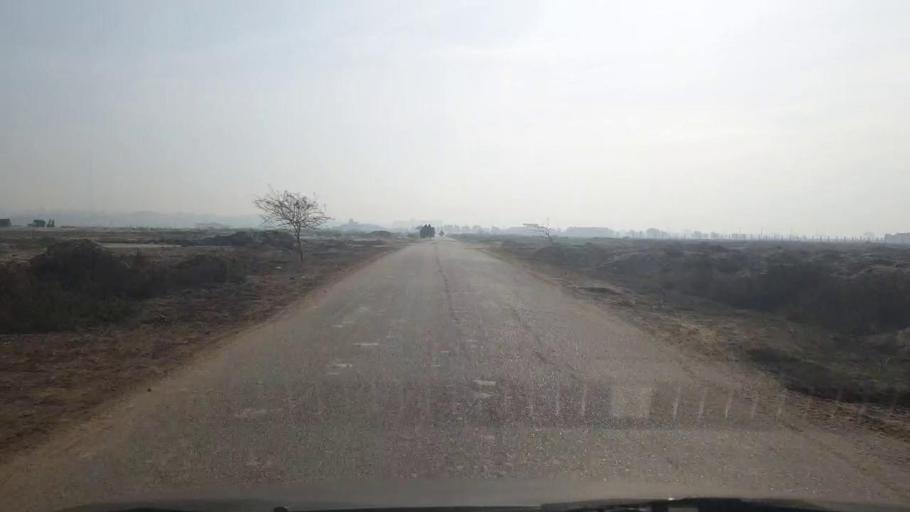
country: PK
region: Sindh
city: Umarkot
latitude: 25.3437
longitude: 69.7120
